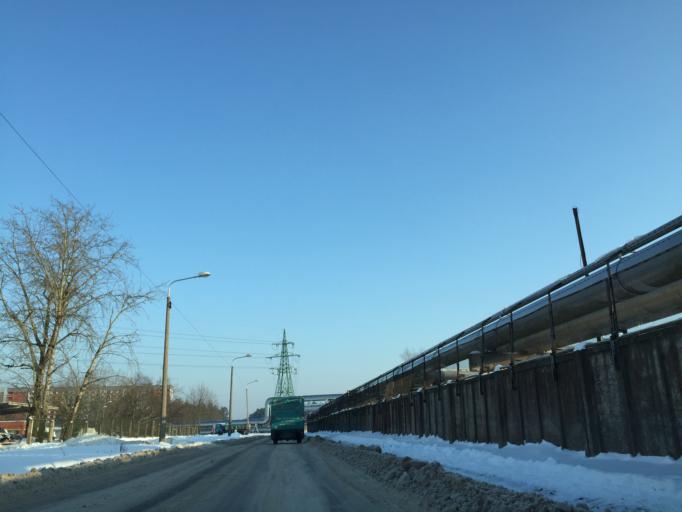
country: LV
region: Stopini
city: Ulbroka
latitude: 56.9301
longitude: 24.2092
